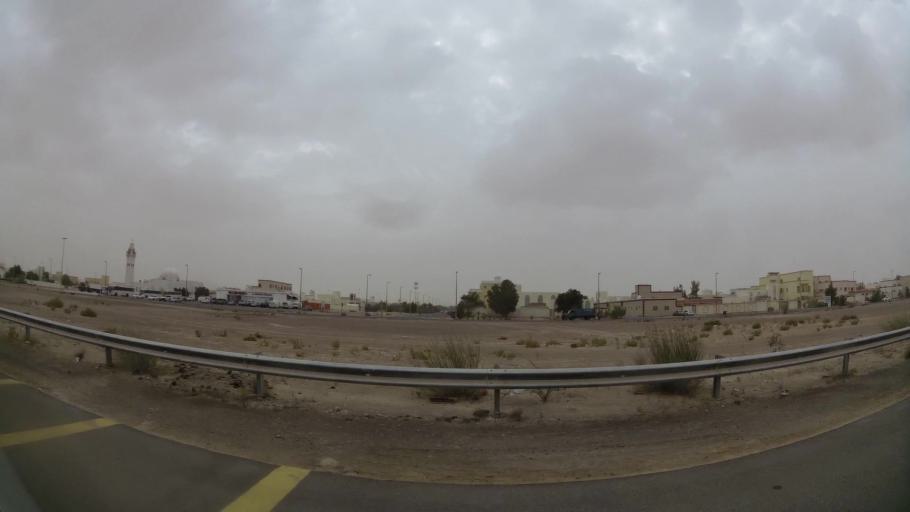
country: AE
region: Abu Dhabi
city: Abu Dhabi
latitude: 24.4018
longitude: 54.7235
